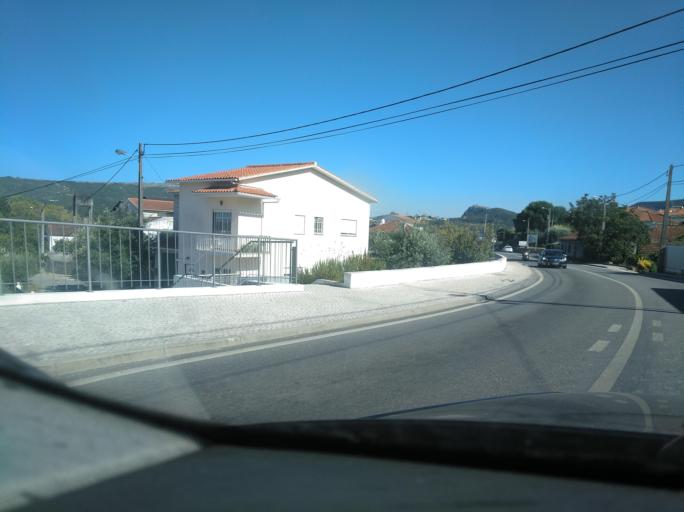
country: PT
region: Leiria
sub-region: Porto de Mos
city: Porto de Mos
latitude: 39.5983
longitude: -8.8295
